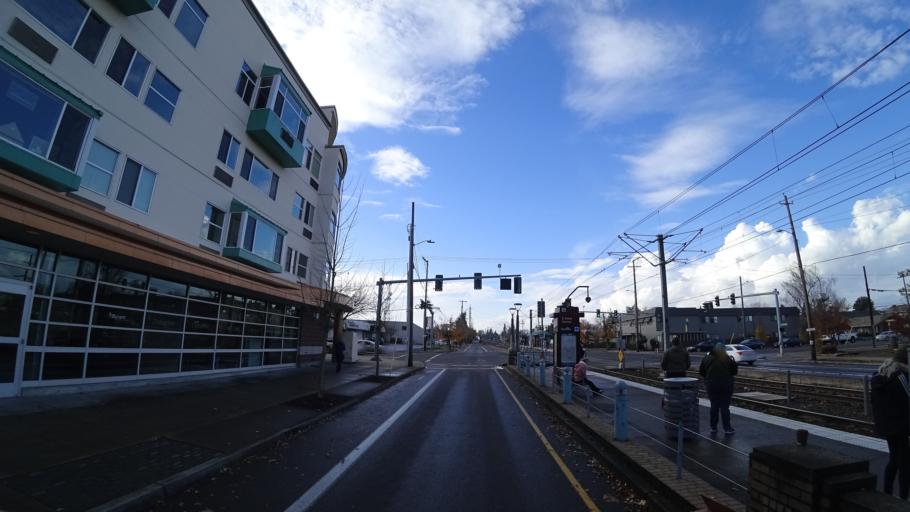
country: US
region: Oregon
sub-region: Multnomah County
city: Lents
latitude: 45.5225
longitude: -122.5578
